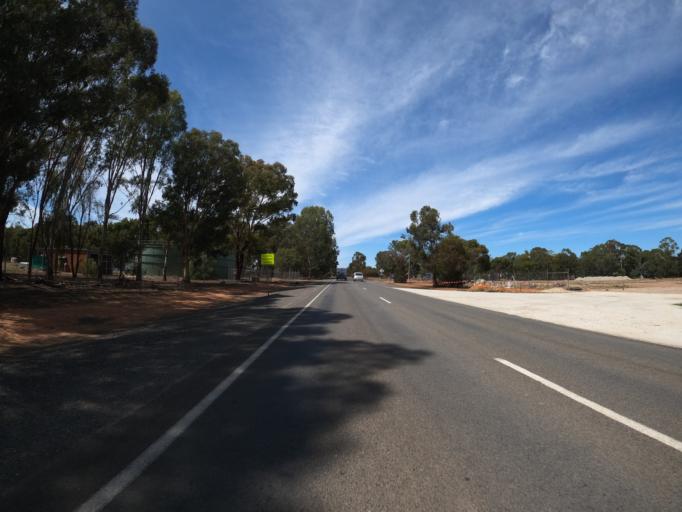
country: AU
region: Victoria
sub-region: Moira
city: Yarrawonga
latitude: -36.0353
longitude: 145.9955
